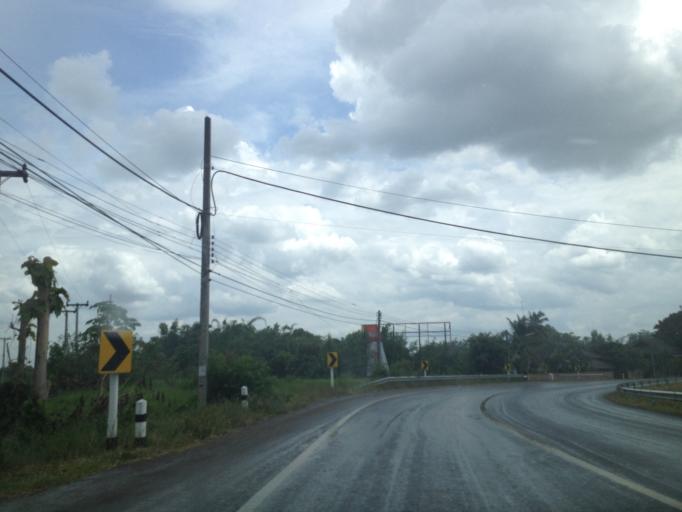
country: TH
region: Chiang Mai
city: San Pa Tong
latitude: 18.6391
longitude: 98.8479
